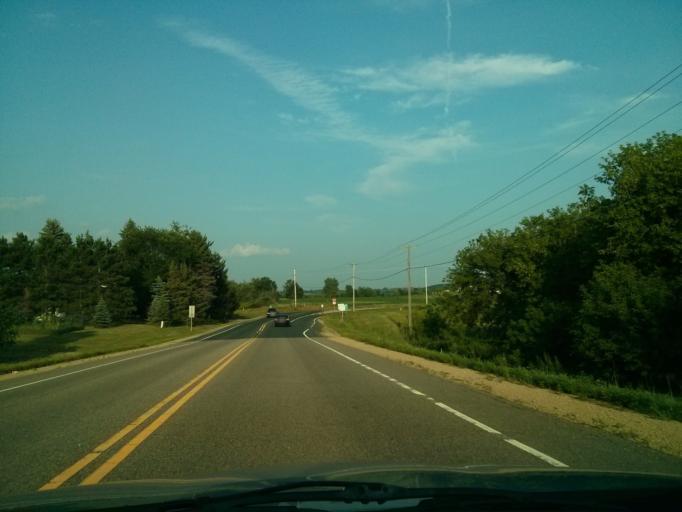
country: US
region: Wisconsin
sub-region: Saint Croix County
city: North Hudson
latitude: 44.9924
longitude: -92.6825
